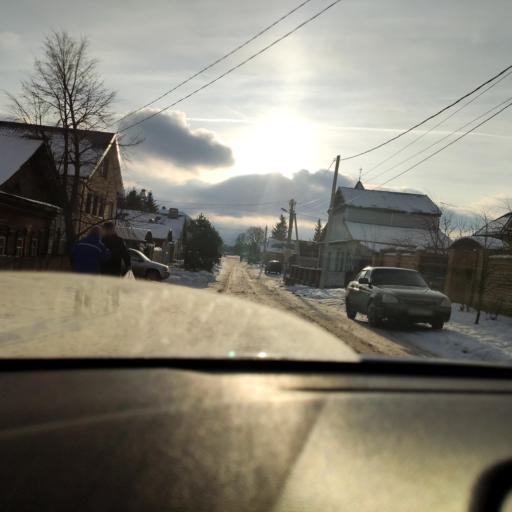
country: RU
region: Tatarstan
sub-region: Gorod Kazan'
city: Kazan
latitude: 55.7949
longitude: 49.0592
